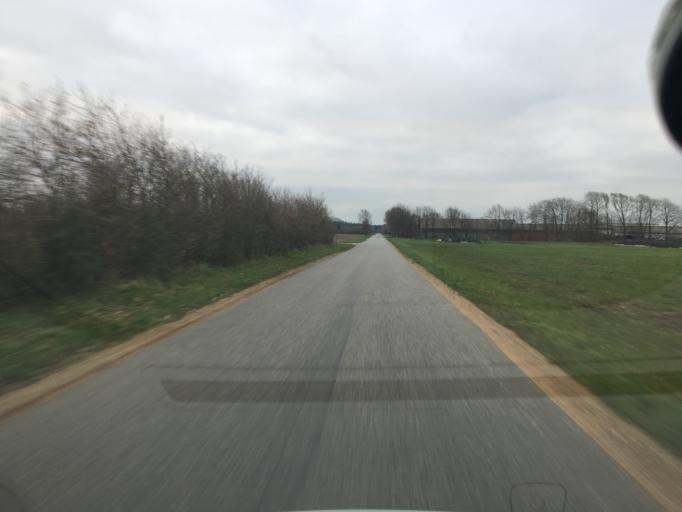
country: DK
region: South Denmark
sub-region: Tonder Kommune
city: Logumkloster
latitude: 55.0319
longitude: 9.0309
